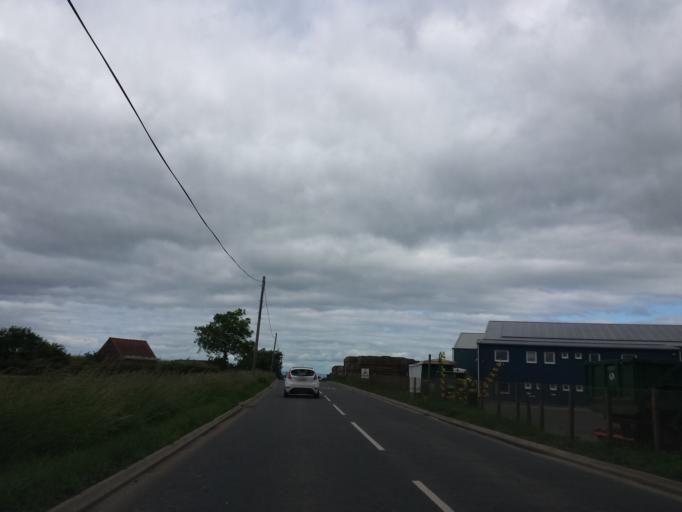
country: GB
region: Scotland
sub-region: East Lothian
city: Haddington
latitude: 55.9726
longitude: -2.8019
